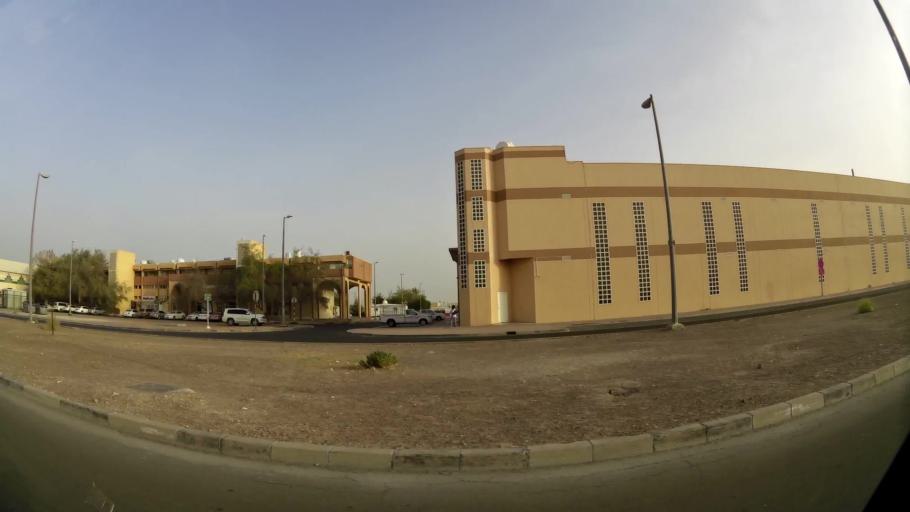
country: OM
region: Al Buraimi
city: Al Buraymi
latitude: 24.2427
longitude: 55.7452
